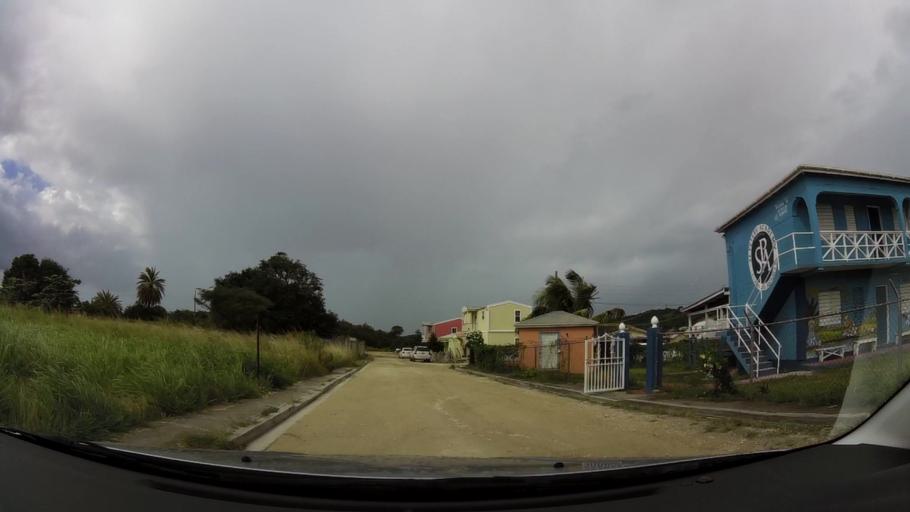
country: AG
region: Saint John
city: Potters Village
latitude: 17.0991
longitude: -61.8254
